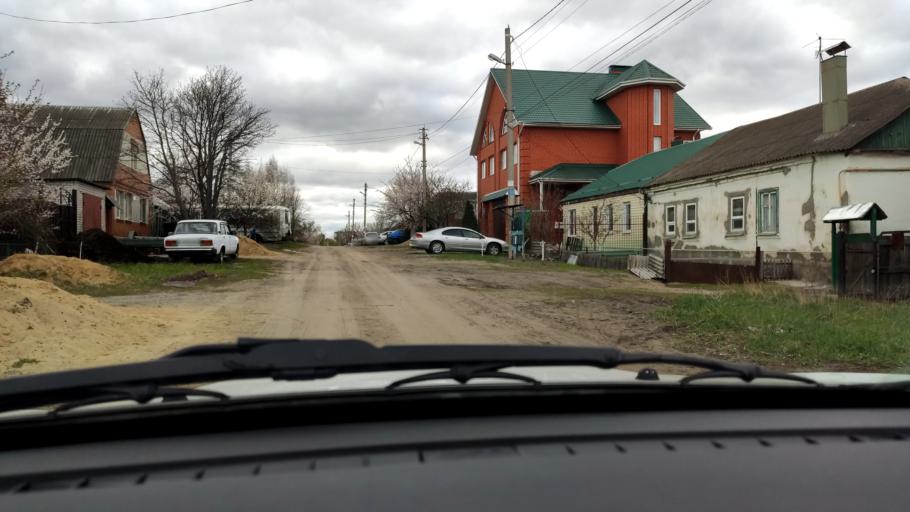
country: RU
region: Voronezj
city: Somovo
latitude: 51.7370
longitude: 39.2696
